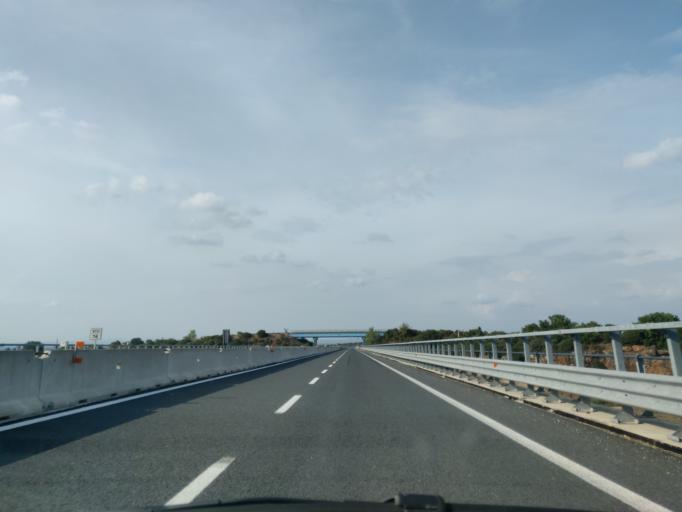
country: IT
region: Latium
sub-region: Provincia di Viterbo
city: Blera
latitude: 42.3420
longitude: 11.9827
